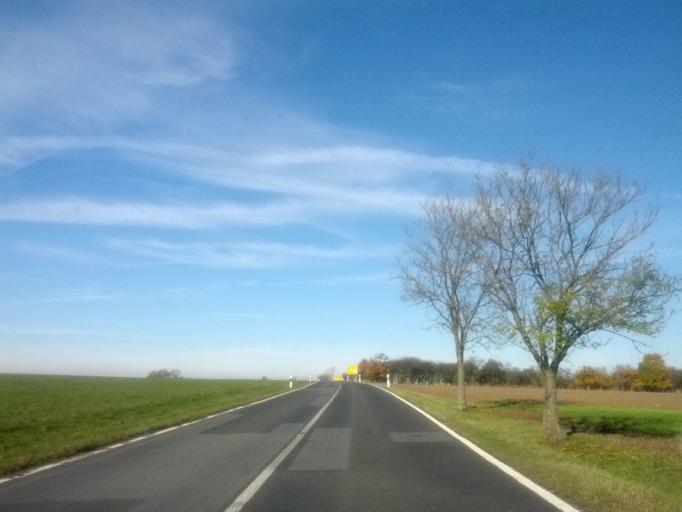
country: DE
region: Thuringia
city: Friedrichswerth
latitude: 50.9618
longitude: 10.5542
